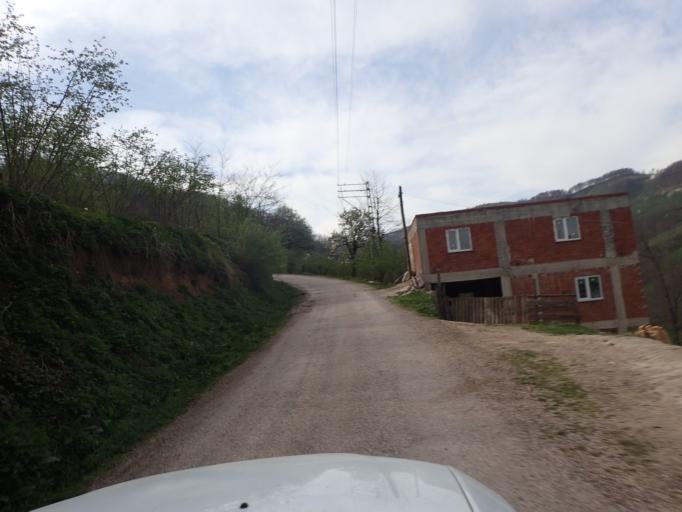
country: TR
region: Ordu
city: Aybasti
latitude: 40.7064
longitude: 37.2808
